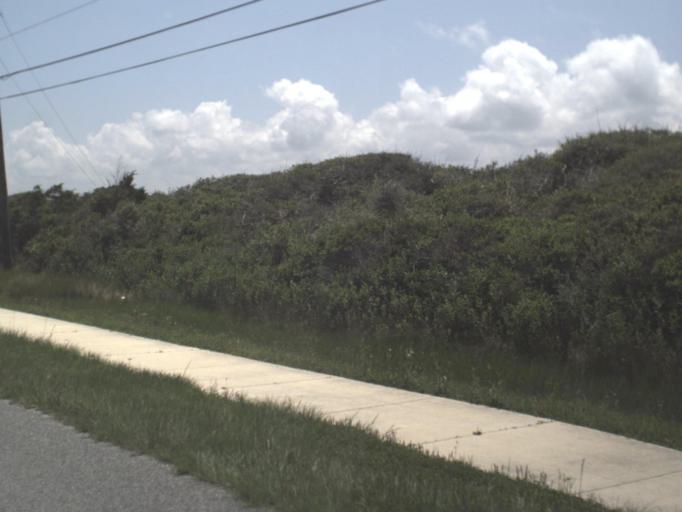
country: US
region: Florida
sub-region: Saint Johns County
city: Butler Beach
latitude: 29.7280
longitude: -81.2384
